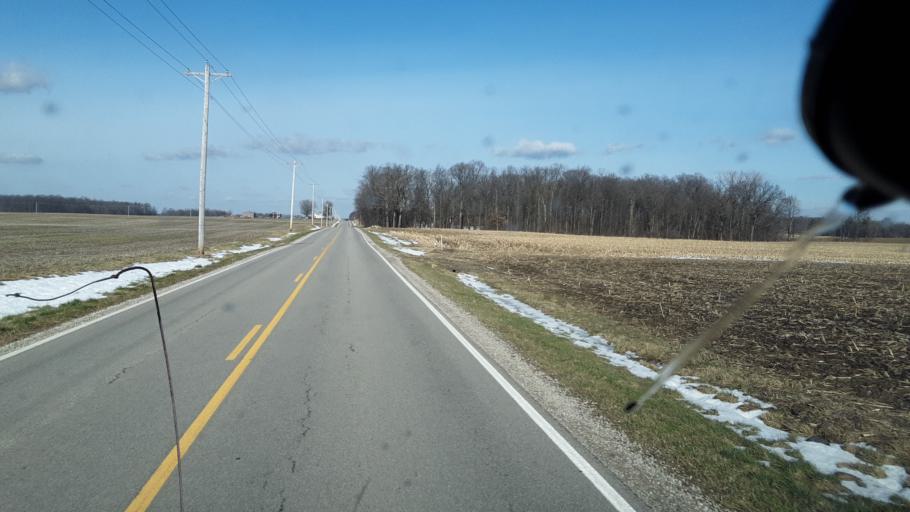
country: US
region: Ohio
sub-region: Huron County
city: Plymouth
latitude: 40.9555
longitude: -82.7433
